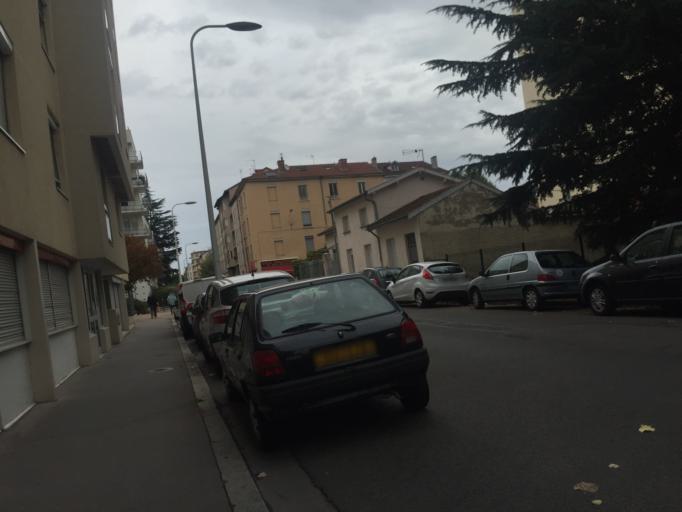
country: FR
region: Rhone-Alpes
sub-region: Departement du Rhone
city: Lyon
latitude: 45.7434
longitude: 4.8629
